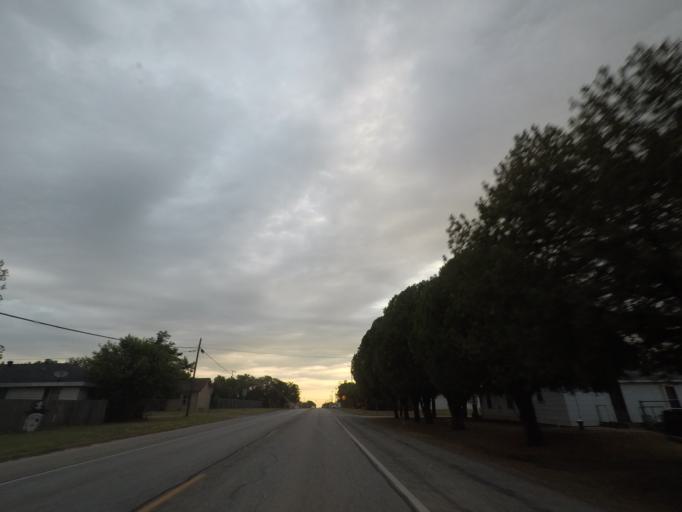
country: US
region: Texas
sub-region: Clay County
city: Henrietta
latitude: 34.0113
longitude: -98.2349
